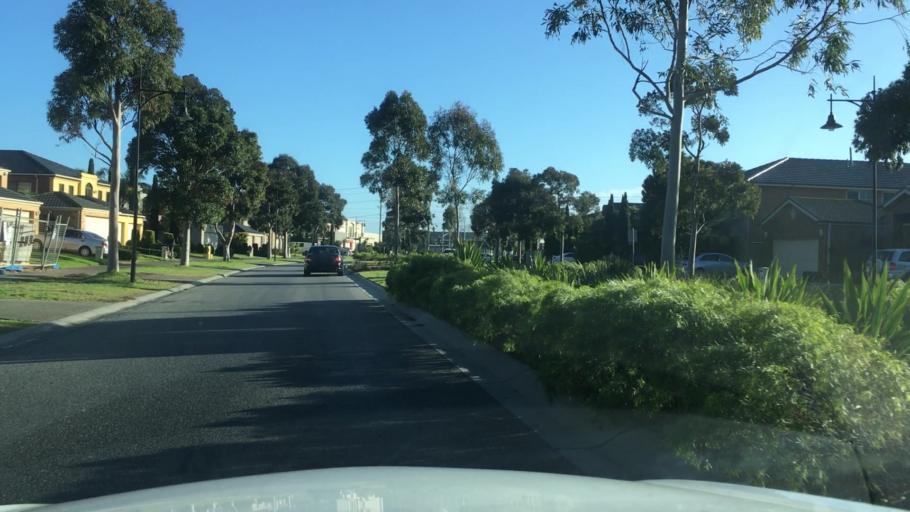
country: AU
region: Victoria
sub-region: Kingston
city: Dingley Village
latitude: -37.9935
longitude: 145.1508
